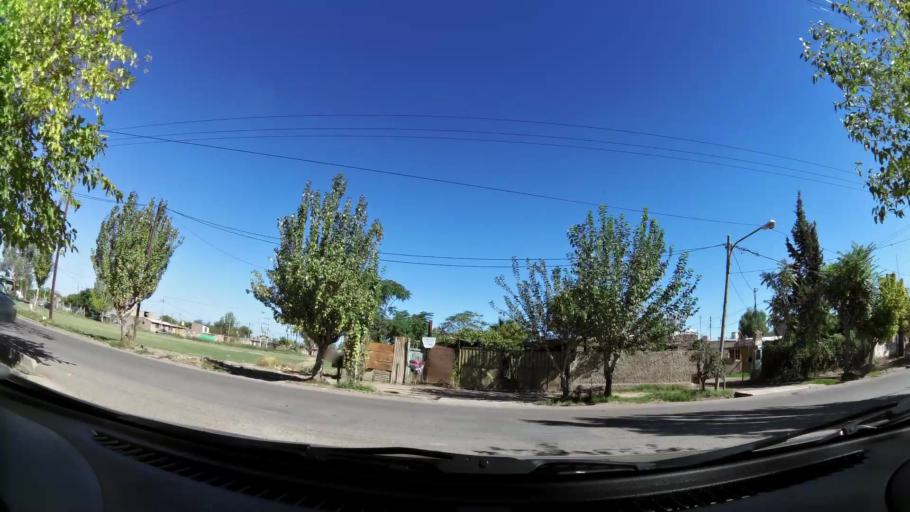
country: AR
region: Mendoza
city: Las Heras
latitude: -32.8273
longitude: -68.8168
